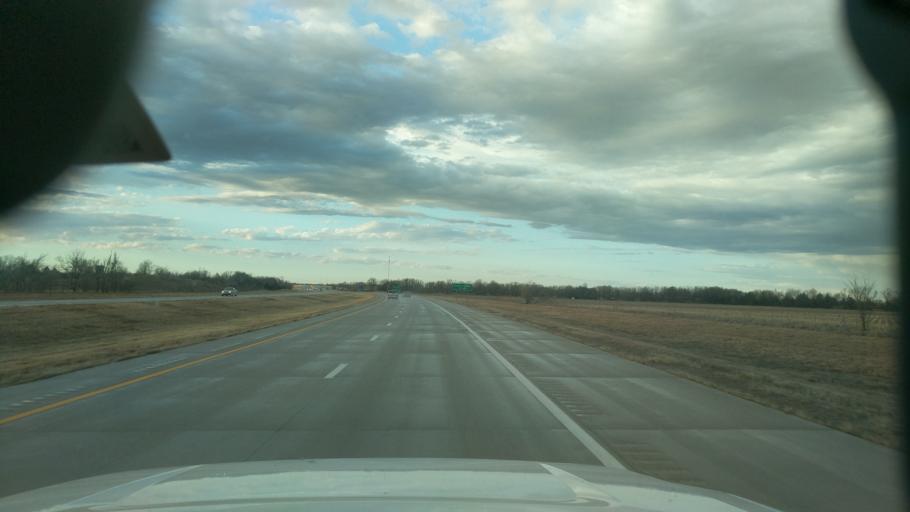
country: US
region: Kansas
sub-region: Harvey County
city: Hesston
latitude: 38.1319
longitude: -97.4023
